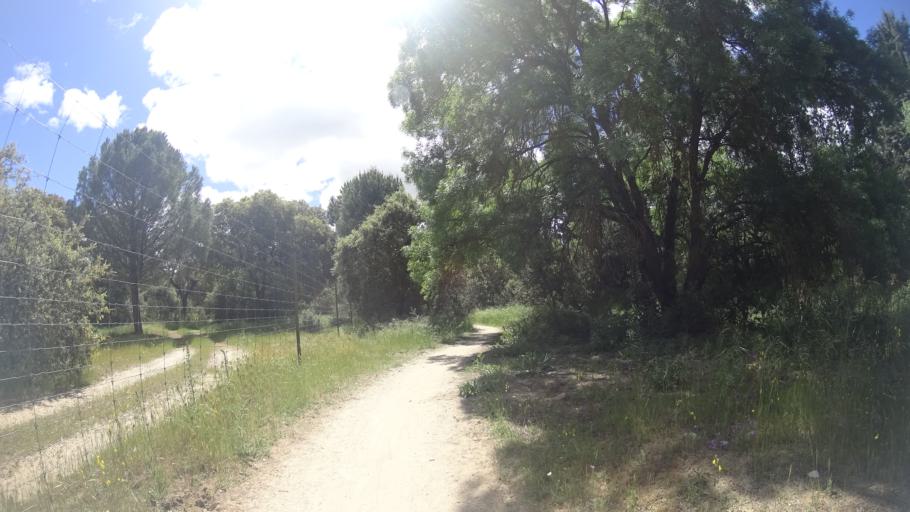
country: ES
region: Madrid
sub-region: Provincia de Madrid
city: Villaviciosa de Odon
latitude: 40.3902
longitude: -3.9429
